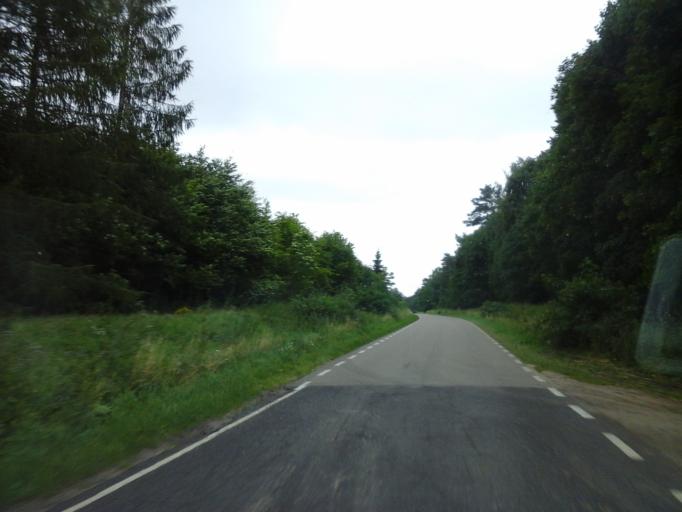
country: PL
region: West Pomeranian Voivodeship
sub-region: Powiat choszczenski
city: Pelczyce
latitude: 53.0949
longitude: 15.2678
